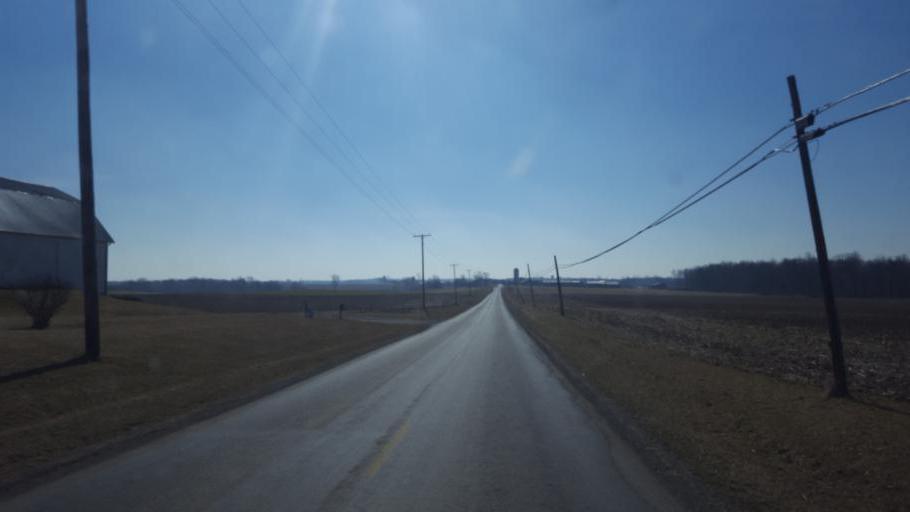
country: US
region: Ohio
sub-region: Richland County
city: Shelby
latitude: 40.9346
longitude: -82.5816
